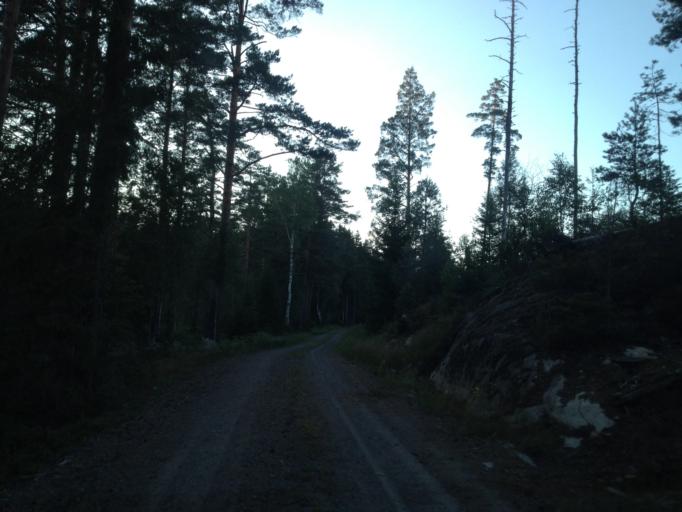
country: SE
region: Kalmar
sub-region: Vasterviks Kommun
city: Overum
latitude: 58.0024
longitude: 16.1224
